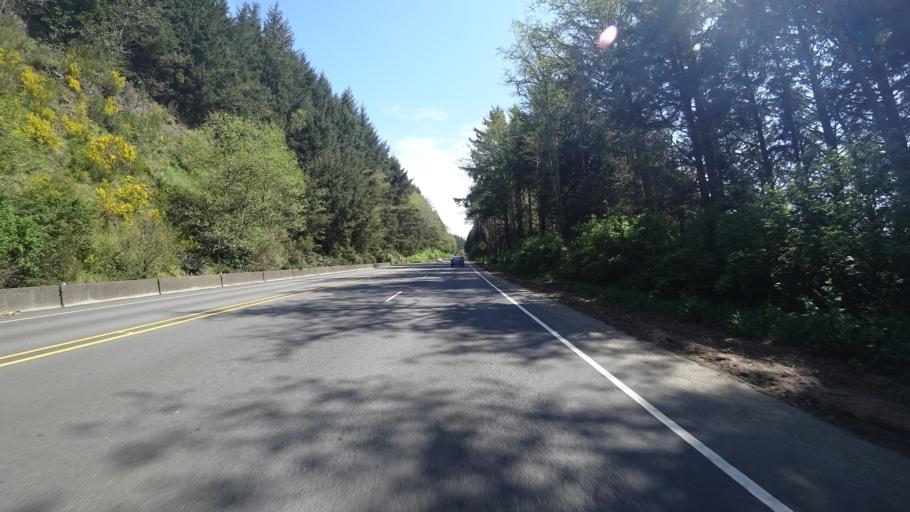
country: US
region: Oregon
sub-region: Lincoln County
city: Depoe Bay
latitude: 44.7681
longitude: -124.0662
